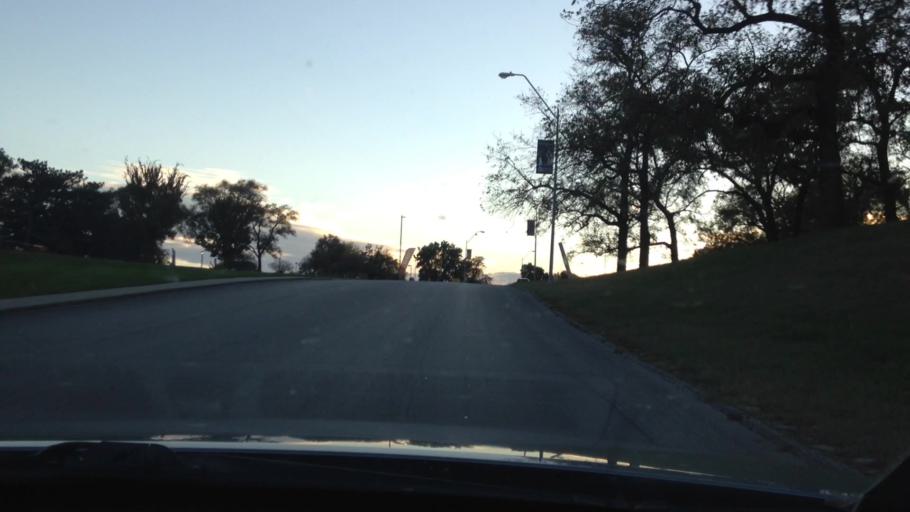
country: US
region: Missouri
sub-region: Jackson County
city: Raytown
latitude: 39.0092
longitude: -94.5328
